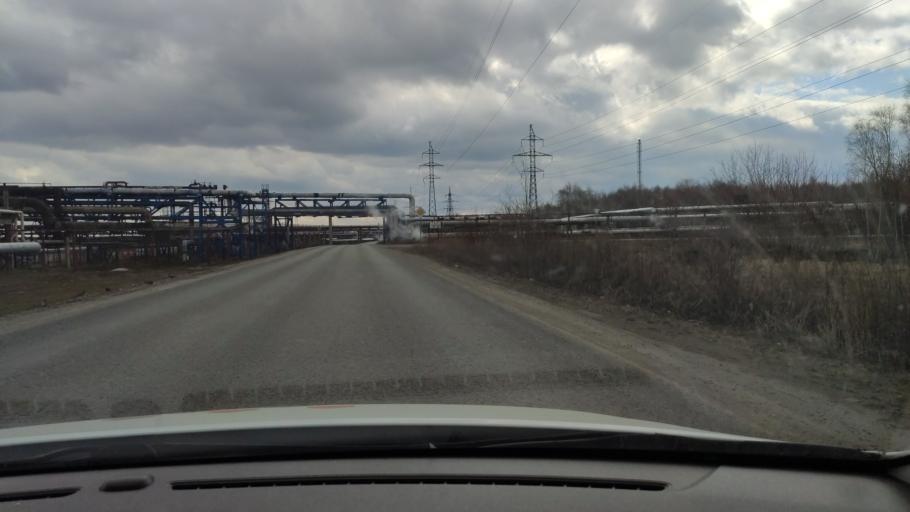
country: RU
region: Tatarstan
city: Staroye Arakchino
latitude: 55.8707
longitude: 48.9739
